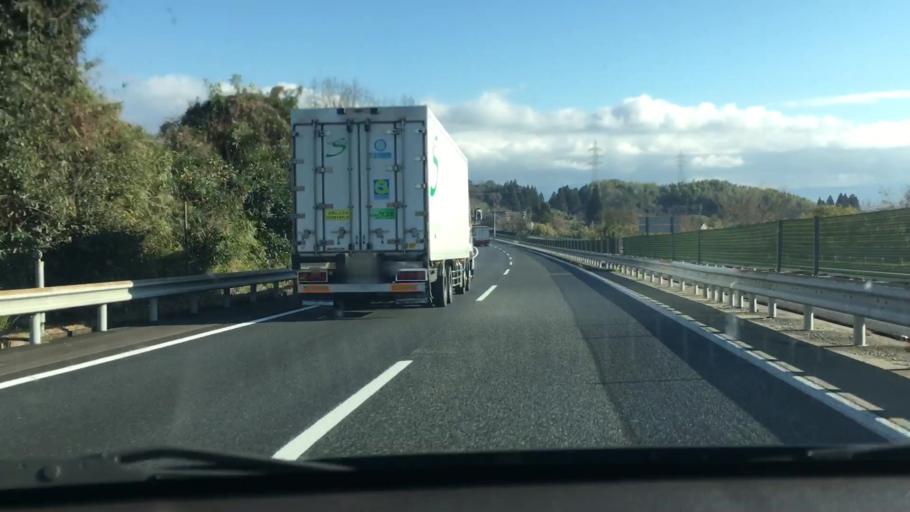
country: JP
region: Kumamoto
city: Hitoyoshi
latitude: 32.2370
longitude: 130.7628
